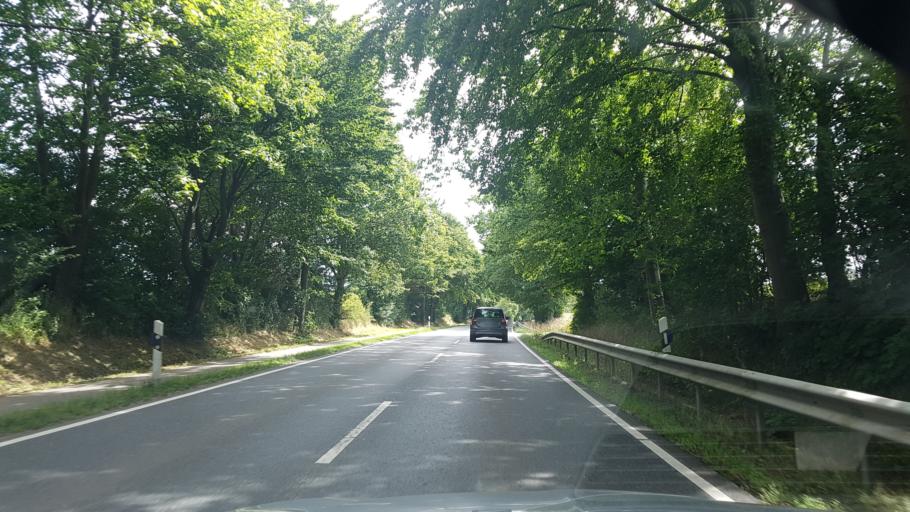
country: DE
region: Schleswig-Holstein
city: Bissee
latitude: 54.1621
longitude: 10.1074
